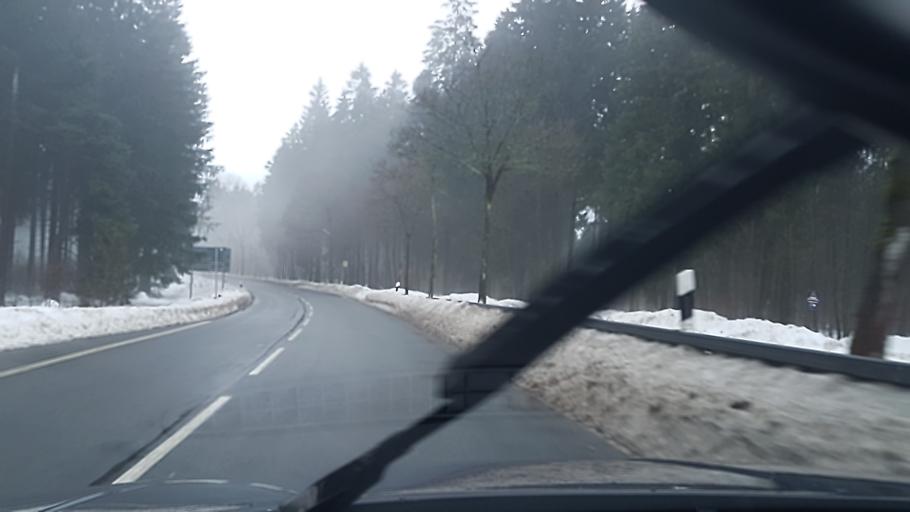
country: DE
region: Lower Saxony
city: Clausthal-Zellerfeld
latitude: 51.8450
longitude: 10.3495
